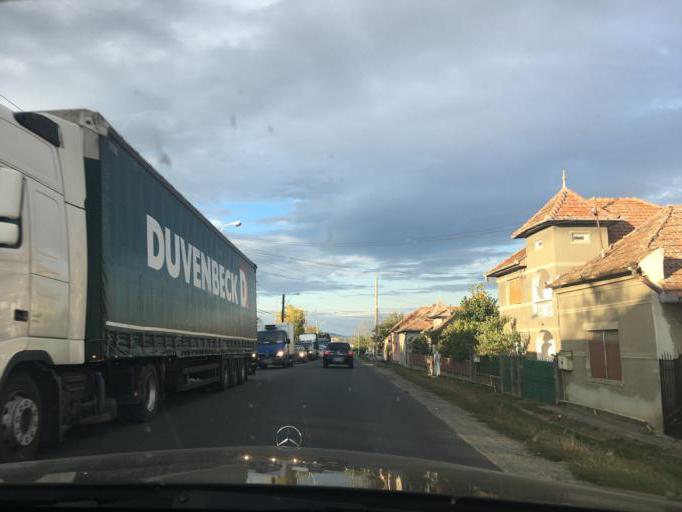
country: RO
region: Alba
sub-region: Oras Teius
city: Teius
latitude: 46.2112
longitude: 23.6769
